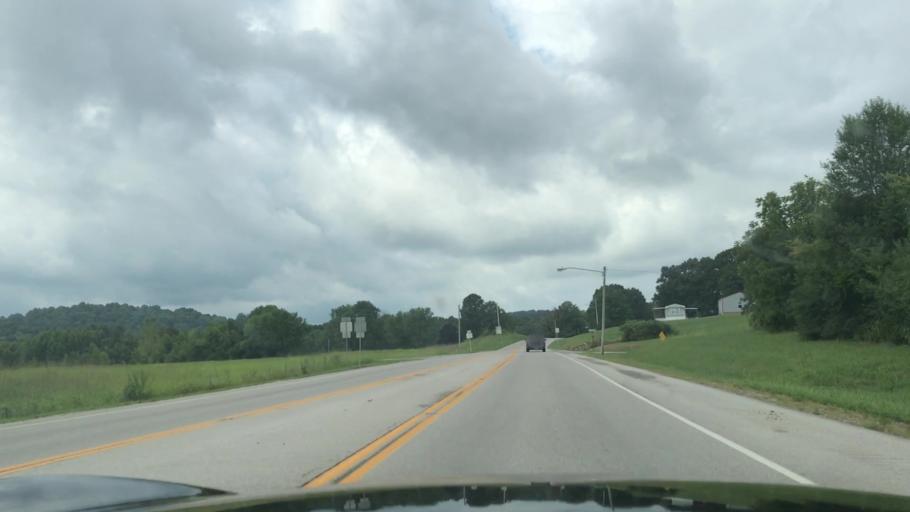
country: US
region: Kentucky
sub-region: Butler County
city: Morgantown
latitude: 37.2134
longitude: -86.7132
